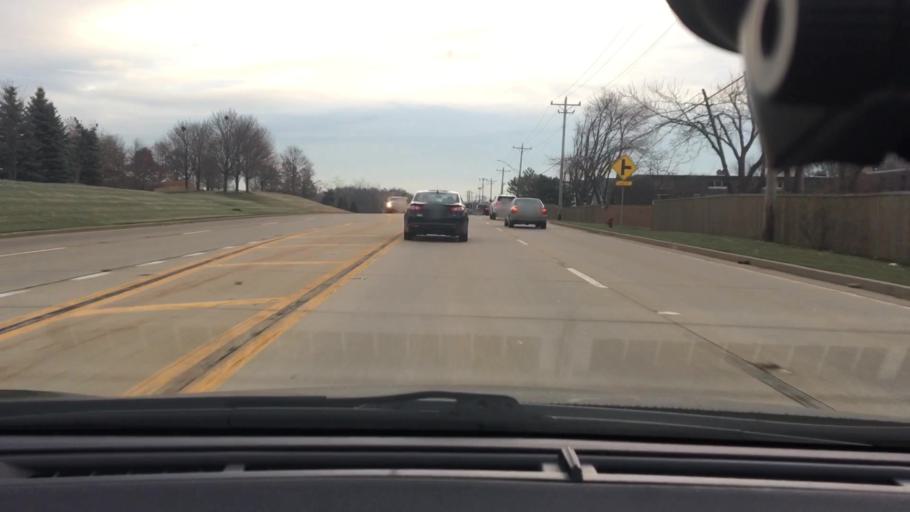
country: US
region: Illinois
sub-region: Lake County
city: Kildeer
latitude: 42.1538
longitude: -88.0483
